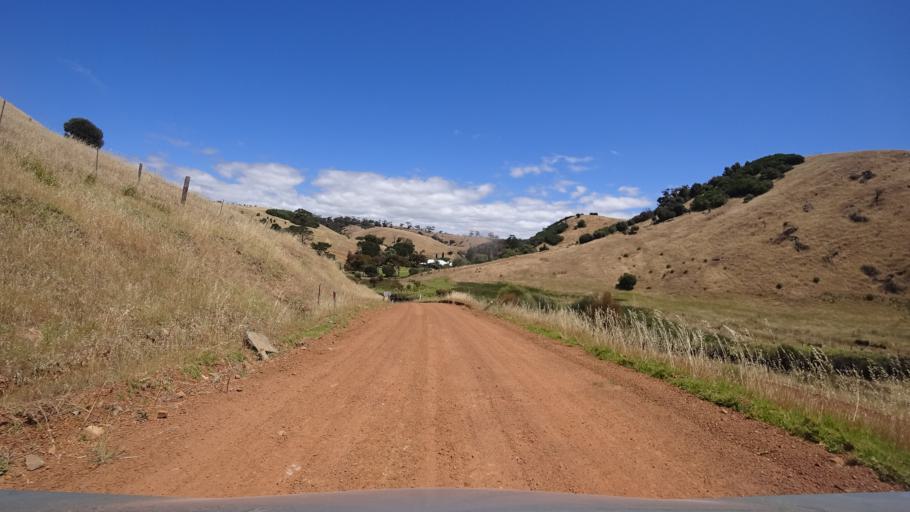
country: AU
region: South Australia
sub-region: Kangaroo Island
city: Kingscote
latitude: -35.6793
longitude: 136.9718
